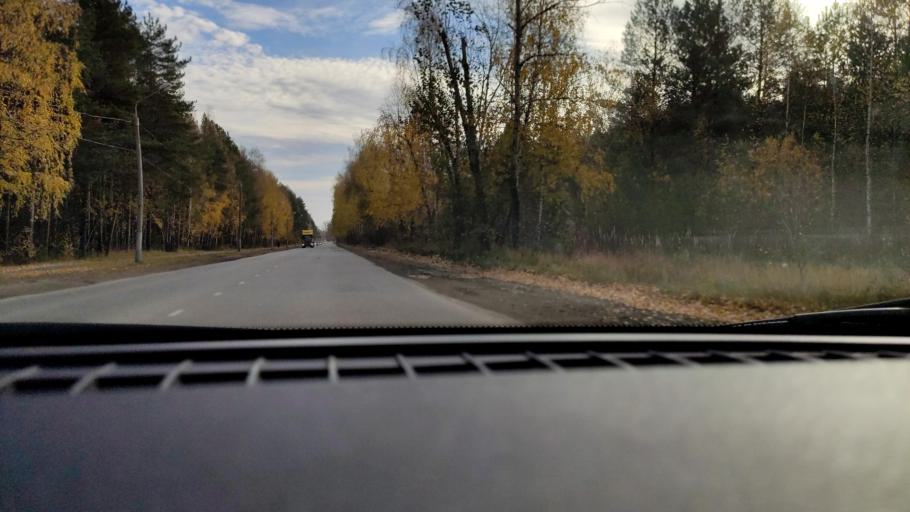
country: RU
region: Perm
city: Overyata
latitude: 58.0142
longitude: 55.9087
